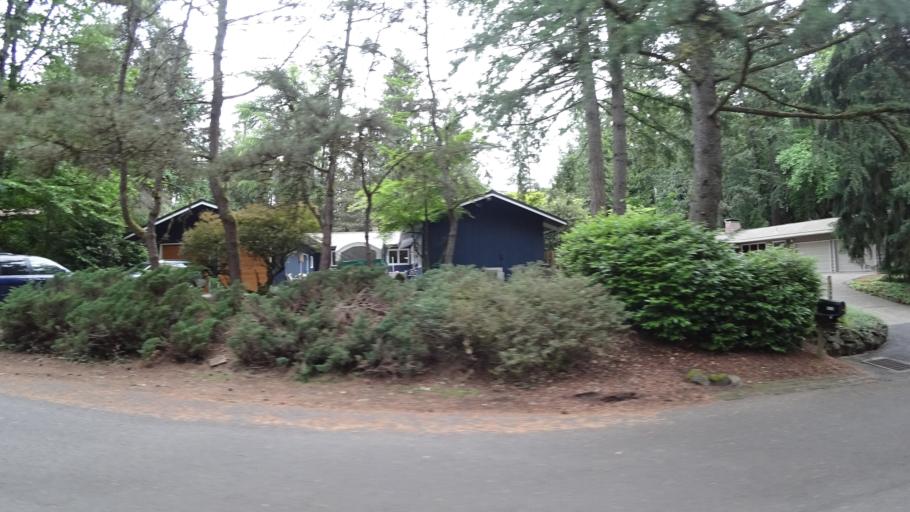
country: US
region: Oregon
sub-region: Washington County
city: Garden Home-Whitford
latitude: 45.4722
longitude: -122.7419
